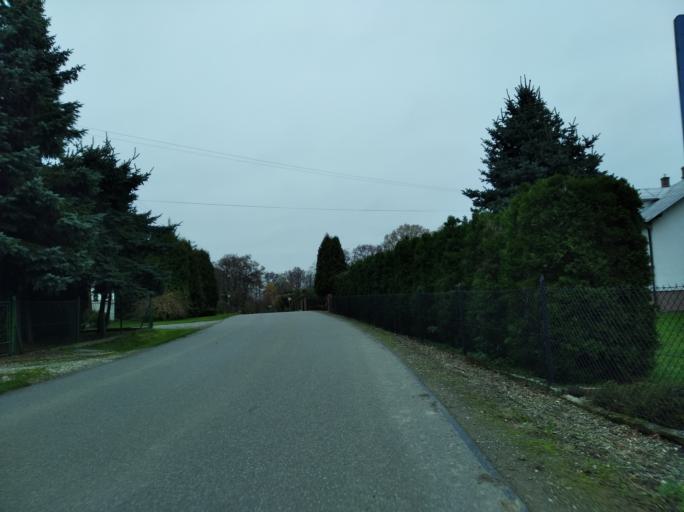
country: PL
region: Subcarpathian Voivodeship
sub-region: Powiat krosnienski
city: Jedlicze
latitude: 49.6903
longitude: 21.6682
